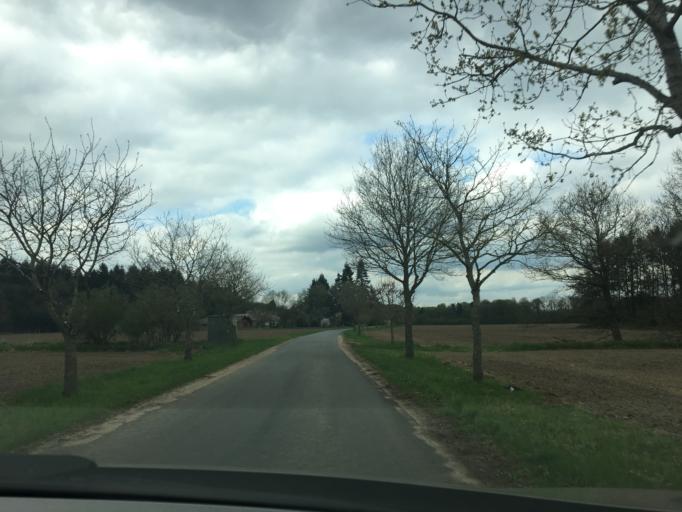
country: DK
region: Central Jutland
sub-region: Horsens Kommune
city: Braedstrup
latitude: 55.9627
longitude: 9.6884
